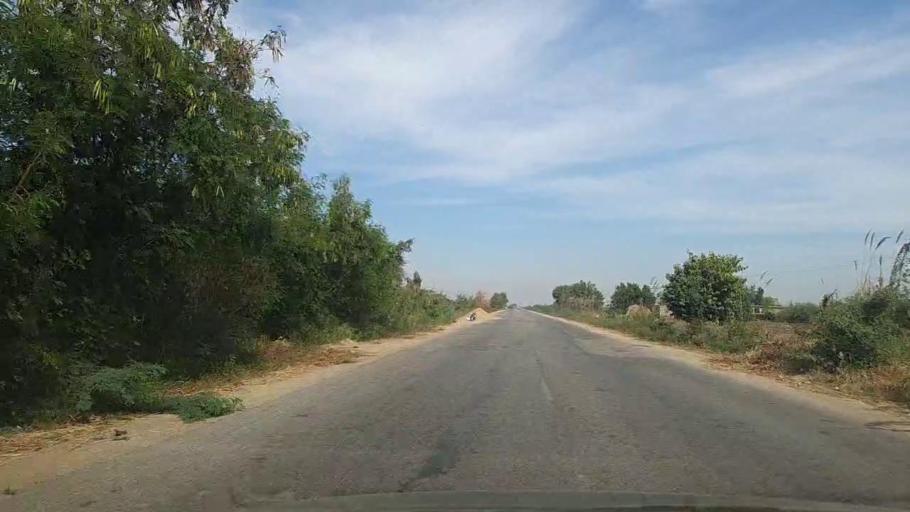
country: PK
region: Sindh
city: Daro Mehar
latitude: 24.9372
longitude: 68.1077
